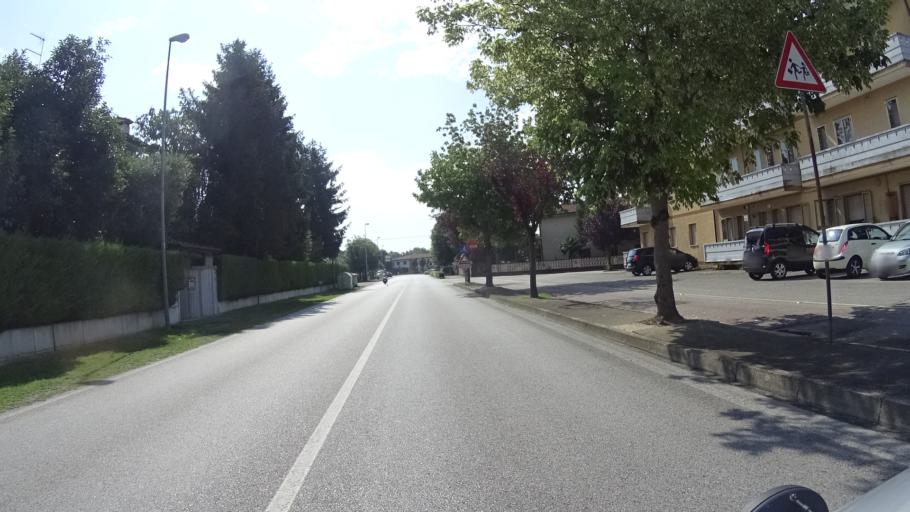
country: IT
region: Friuli Venezia Giulia
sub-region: Provincia di Udine
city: Latisana
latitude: 45.7728
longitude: 13.0170
